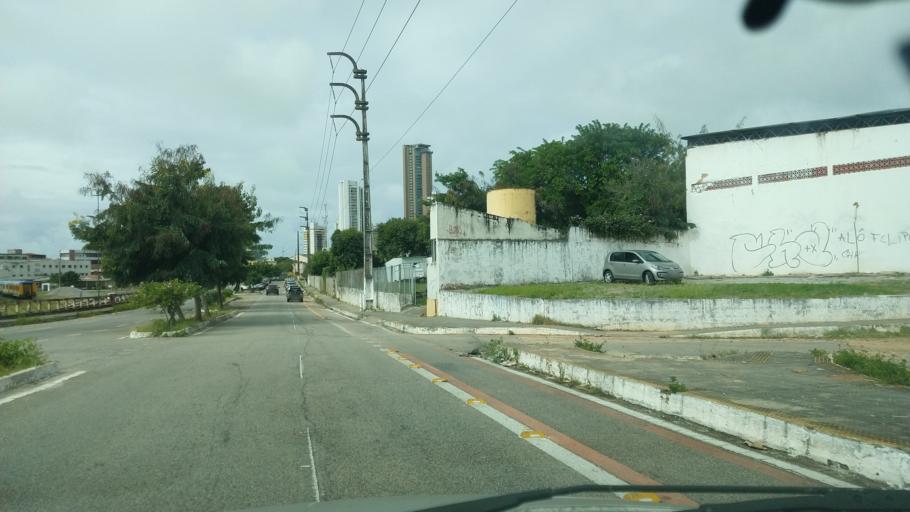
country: BR
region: Rio Grande do Norte
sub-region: Natal
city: Natal
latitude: -5.7817
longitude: -35.2083
